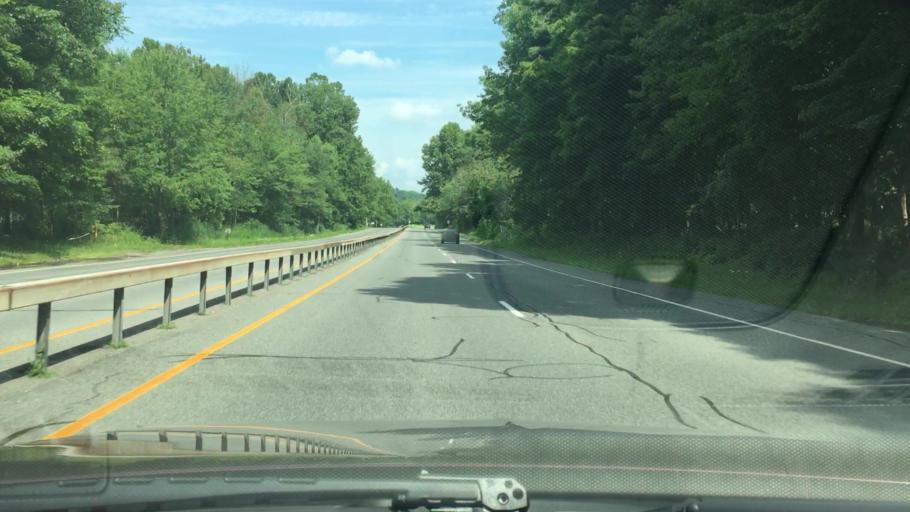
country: US
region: New York
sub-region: Dutchess County
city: Brinckerhoff
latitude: 41.5386
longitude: -73.8132
